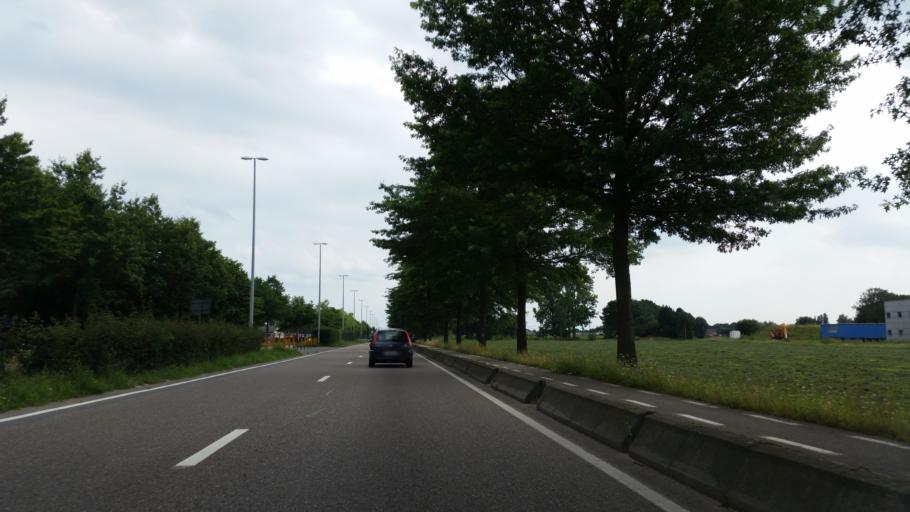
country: BE
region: Flanders
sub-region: Provincie Antwerpen
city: Geel
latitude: 51.1583
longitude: 4.9693
